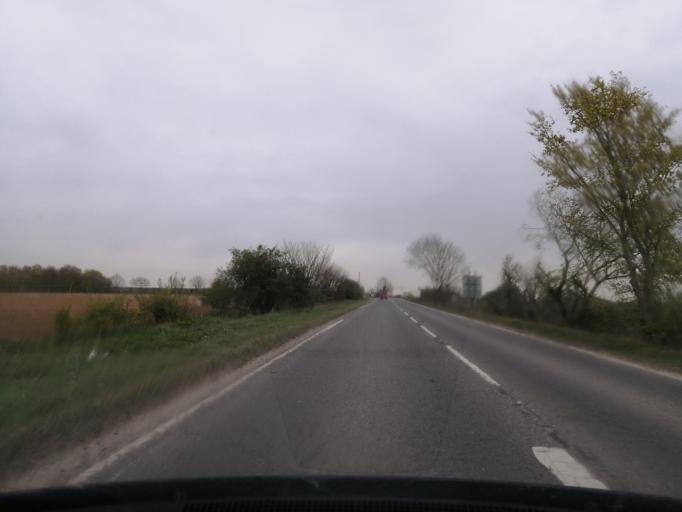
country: GB
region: England
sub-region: Peterborough
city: Thornhaugh
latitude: 52.5852
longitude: -0.4351
